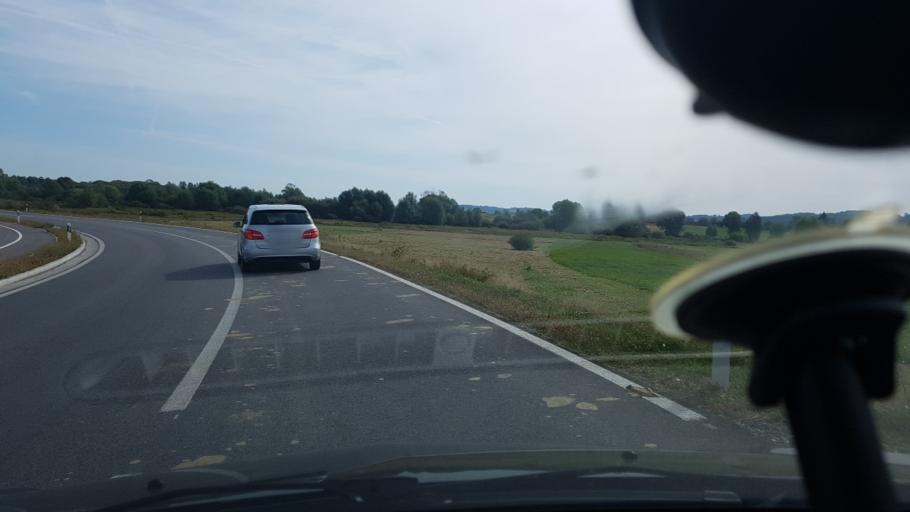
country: HR
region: Krapinsko-Zagorska
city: Marija Bistrica
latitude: 46.0532
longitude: 16.1501
